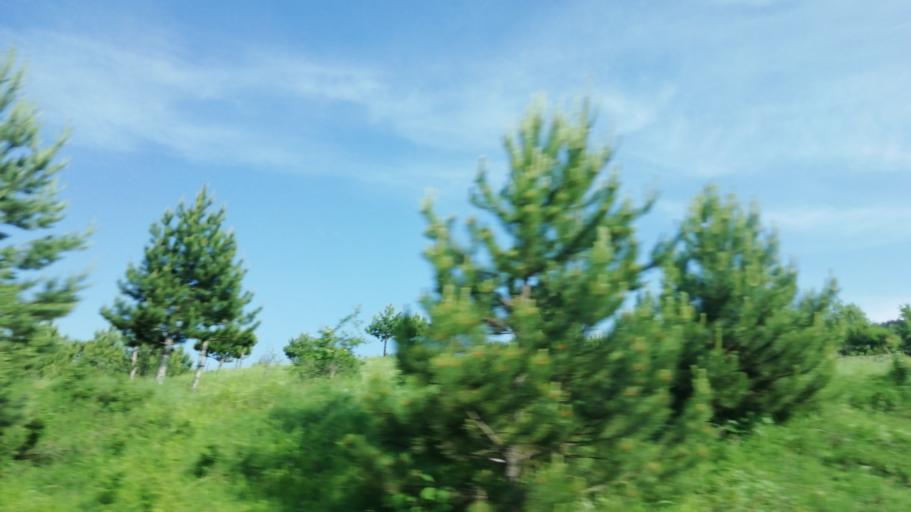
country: TR
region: Karabuk
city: Karabuk
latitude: 41.0875
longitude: 32.5836
